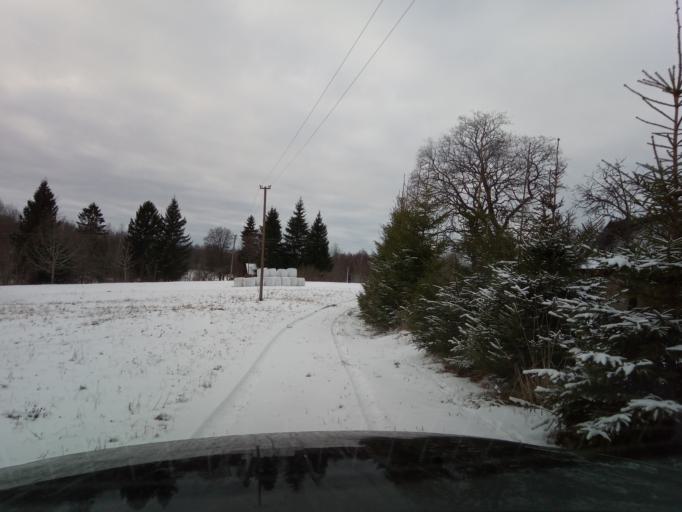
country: LT
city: Zarasai
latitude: 55.7298
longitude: 25.9533
